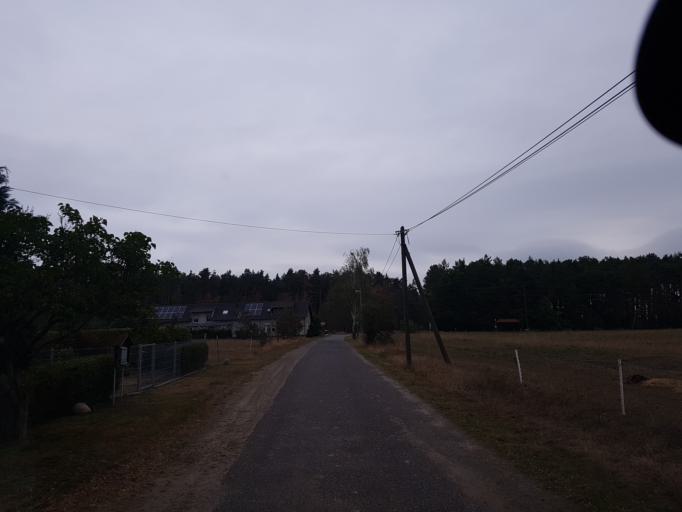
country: DE
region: Brandenburg
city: Crinitz
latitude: 51.7174
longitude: 13.8244
